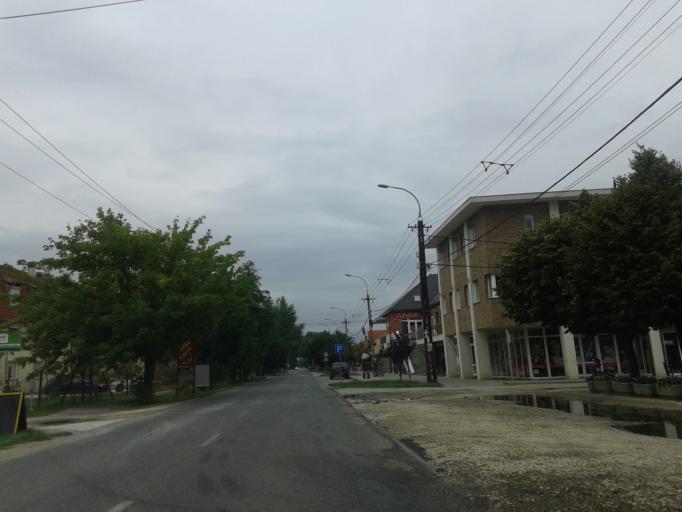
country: HU
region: Pest
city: Halasztelek
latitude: 47.3601
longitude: 18.9874
